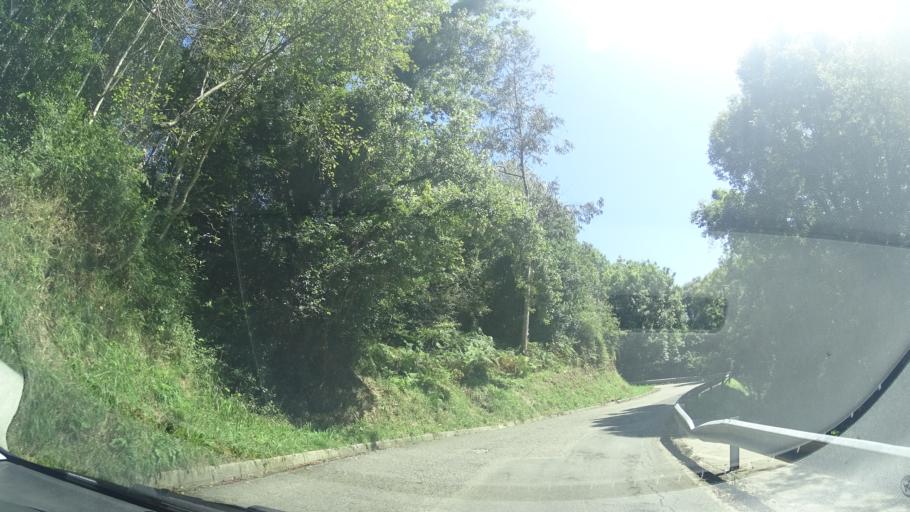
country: ES
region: Asturias
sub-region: Province of Asturias
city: Ribadesella
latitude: 43.4431
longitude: -5.0903
